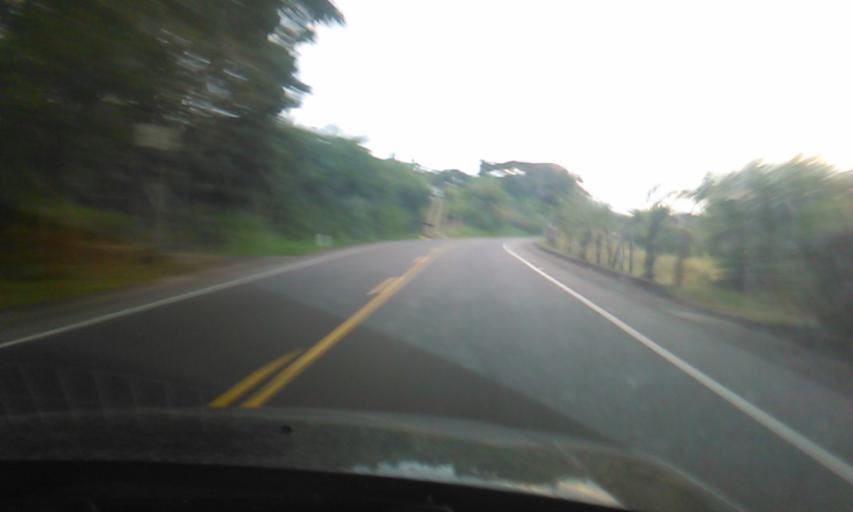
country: CO
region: Quindio
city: La Tebaida
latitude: 4.4283
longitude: -75.8609
